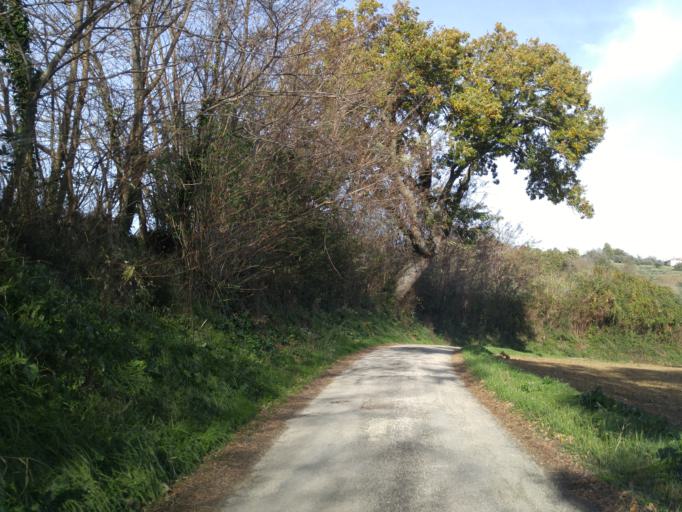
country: IT
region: The Marches
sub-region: Provincia di Pesaro e Urbino
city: Saltara
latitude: 43.7613
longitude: 12.9005
